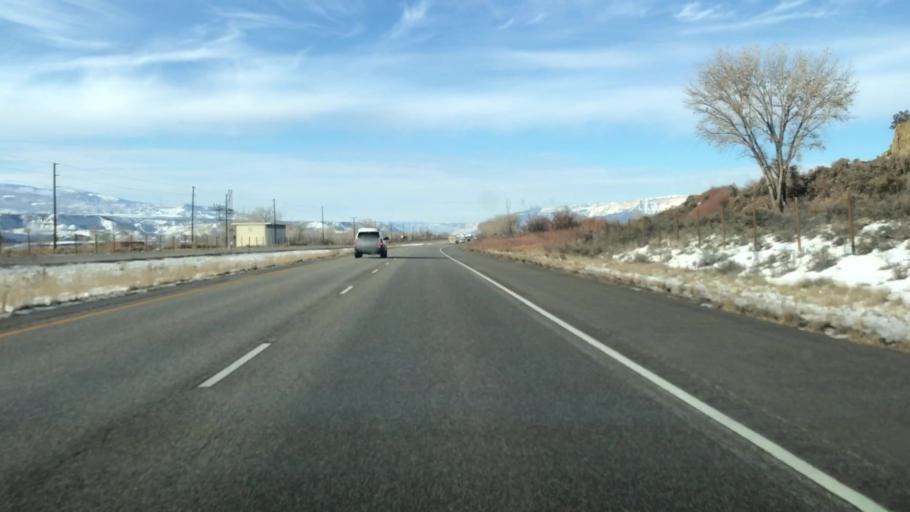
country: US
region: Colorado
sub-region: Garfield County
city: Silt
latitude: 39.5459
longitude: -107.6259
